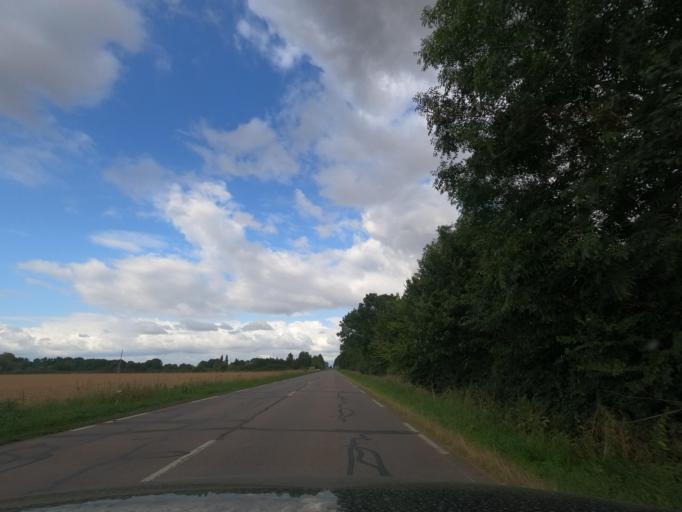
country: FR
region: Lower Normandy
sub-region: Departement du Calvados
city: Orbec
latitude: 48.9515
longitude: 0.4619
